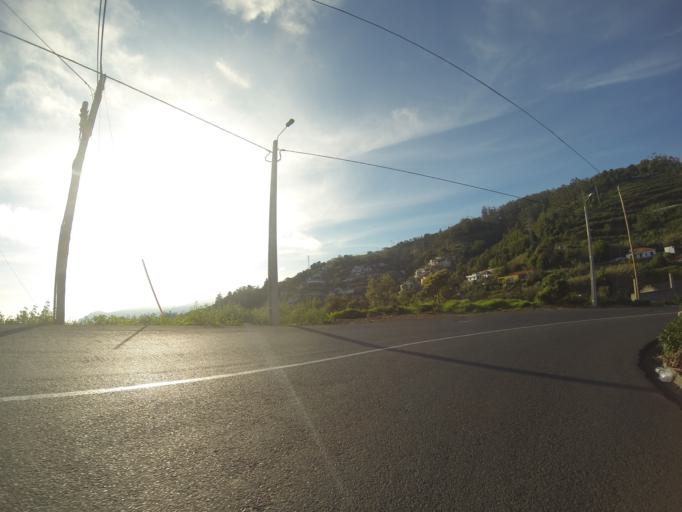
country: PT
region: Madeira
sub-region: Funchal
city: Nossa Senhora do Monte
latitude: 32.6604
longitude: -16.8750
